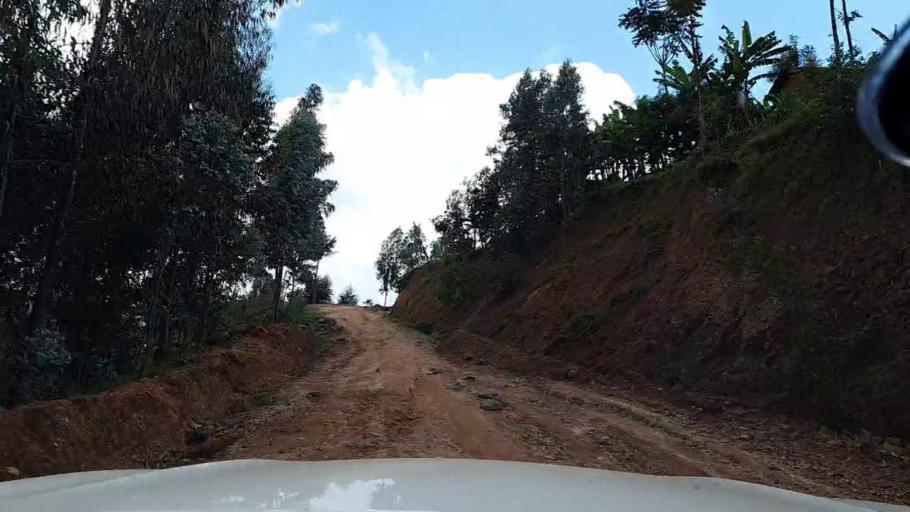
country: RW
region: Southern Province
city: Nzega
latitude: -2.7030
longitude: 29.4334
